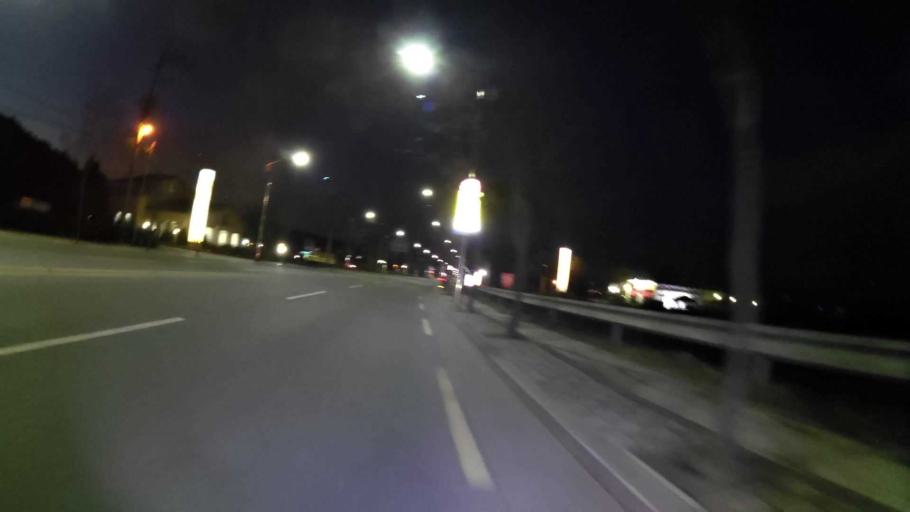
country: KR
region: Gyeongsangbuk-do
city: Gyeongsan-si
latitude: 35.8556
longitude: 128.6796
